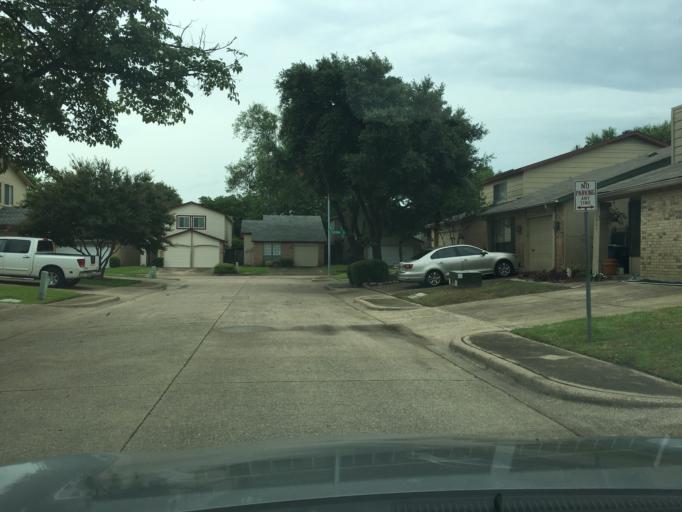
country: US
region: Texas
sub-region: Dallas County
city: Garland
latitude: 32.9501
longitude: -96.6704
